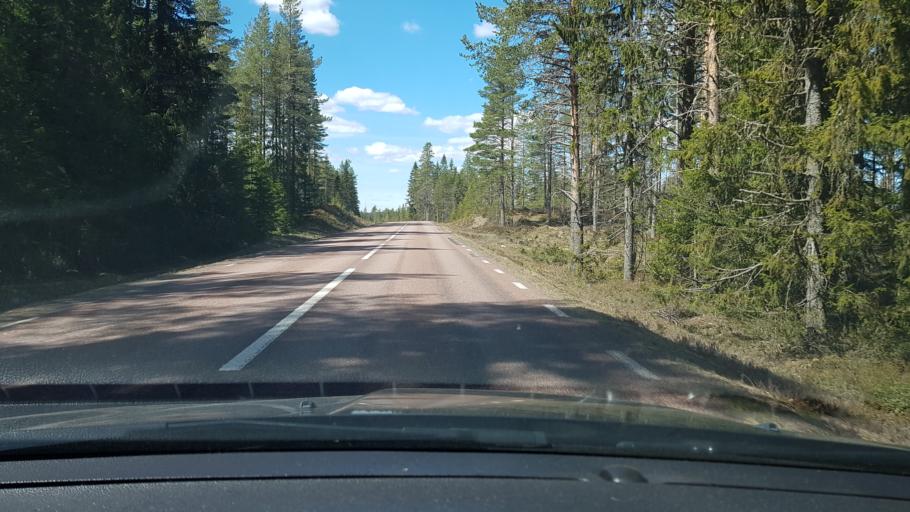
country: SE
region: Dalarna
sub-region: Malung-Saelens kommun
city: Malung
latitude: 61.0509
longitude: 13.4024
